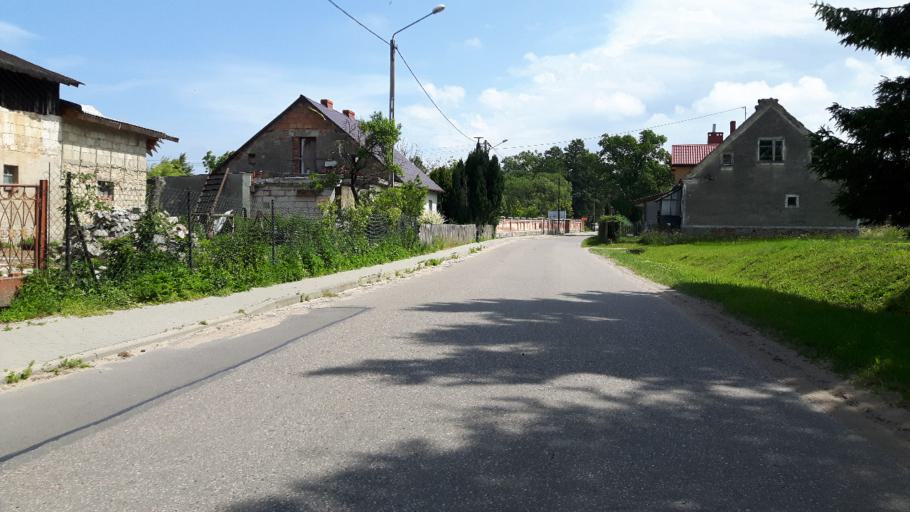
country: PL
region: Pomeranian Voivodeship
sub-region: Powiat wejherowski
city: Choczewo
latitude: 54.7564
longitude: 17.7849
